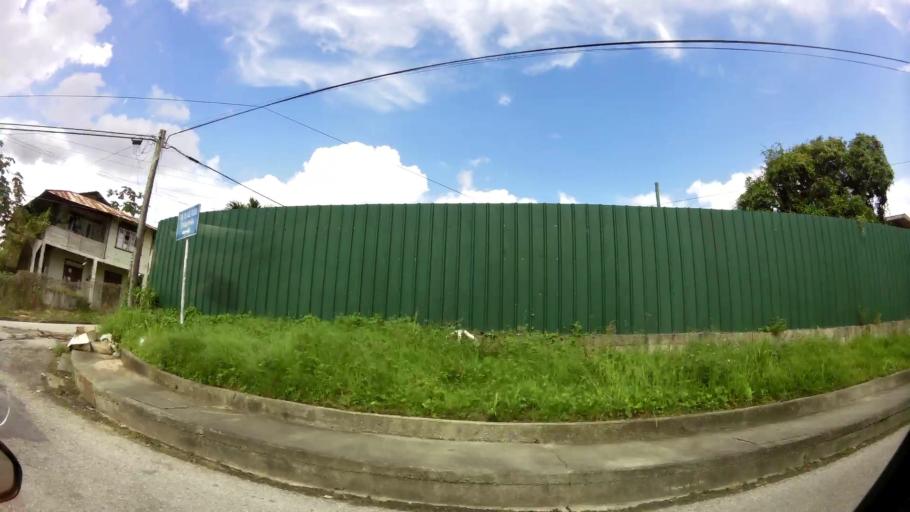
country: TT
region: City of San Fernando
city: Mon Repos
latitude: 10.2740
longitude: -61.4503
